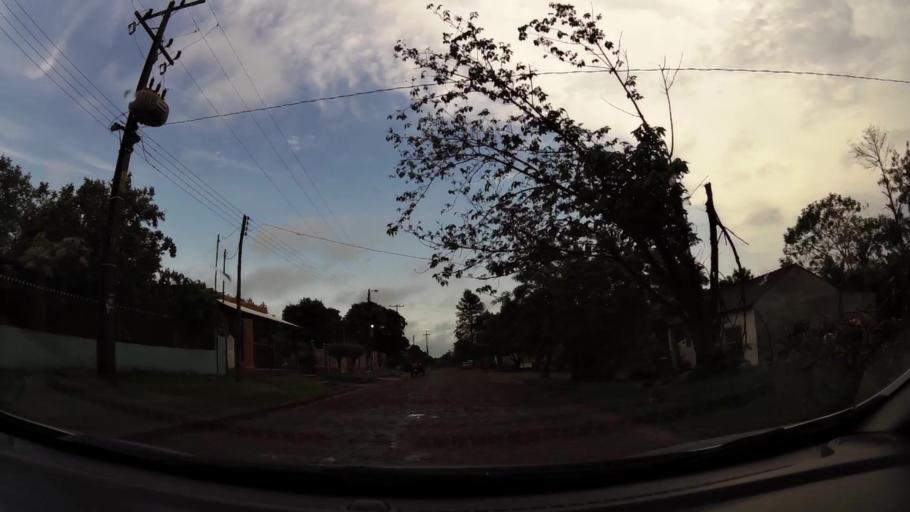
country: PY
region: Alto Parana
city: Presidente Franco
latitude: -25.5336
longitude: -54.6684
